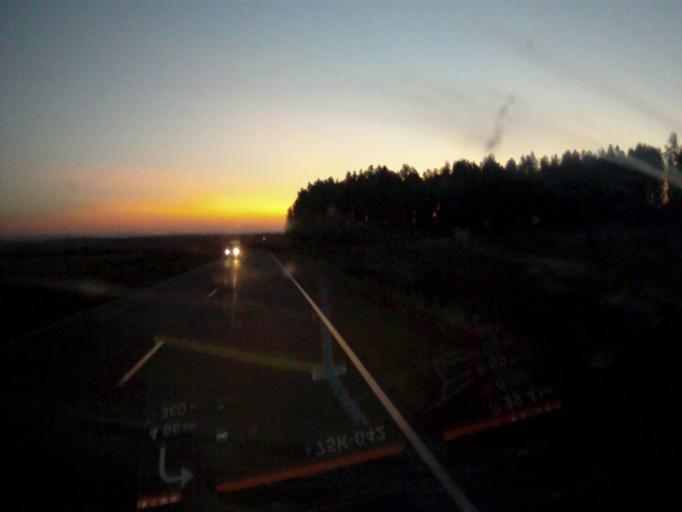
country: RU
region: Chelyabinsk
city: Timiryazevskiy
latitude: 55.2095
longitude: 60.6674
